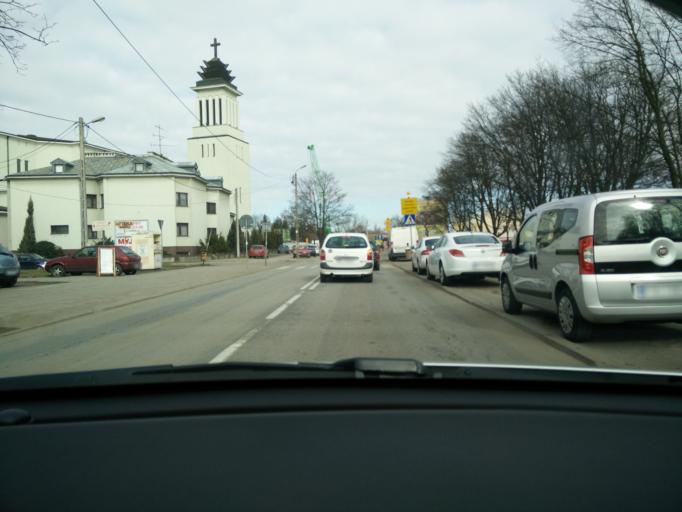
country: PL
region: Greater Poland Voivodeship
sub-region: Powiat poznanski
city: Lubon
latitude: 52.3685
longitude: 16.9038
